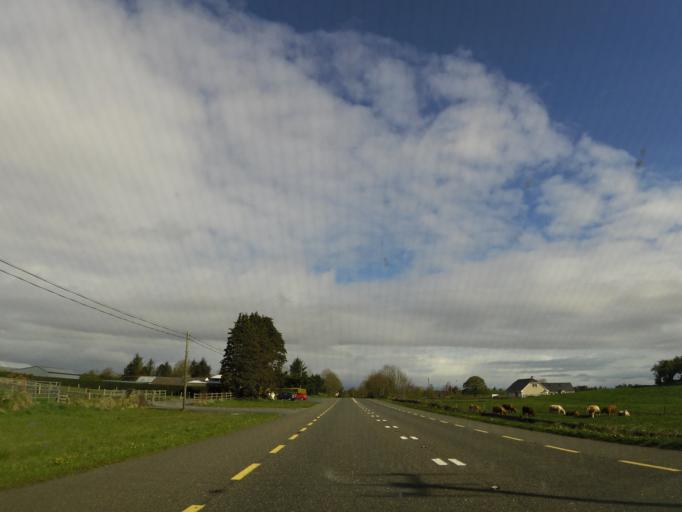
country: IE
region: Connaught
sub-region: Sligo
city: Tobercurry
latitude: 53.9307
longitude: -8.7855
